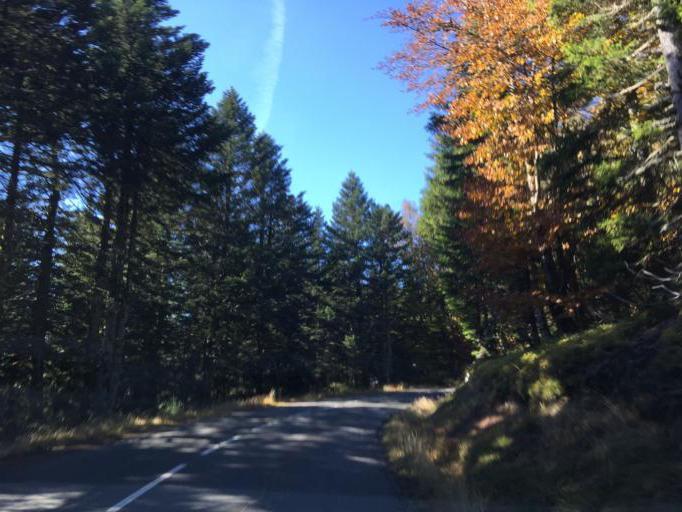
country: FR
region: Rhone-Alpes
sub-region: Departement de la Loire
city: Saint-Julien-Molin-Molette
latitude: 45.3779
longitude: 4.5635
